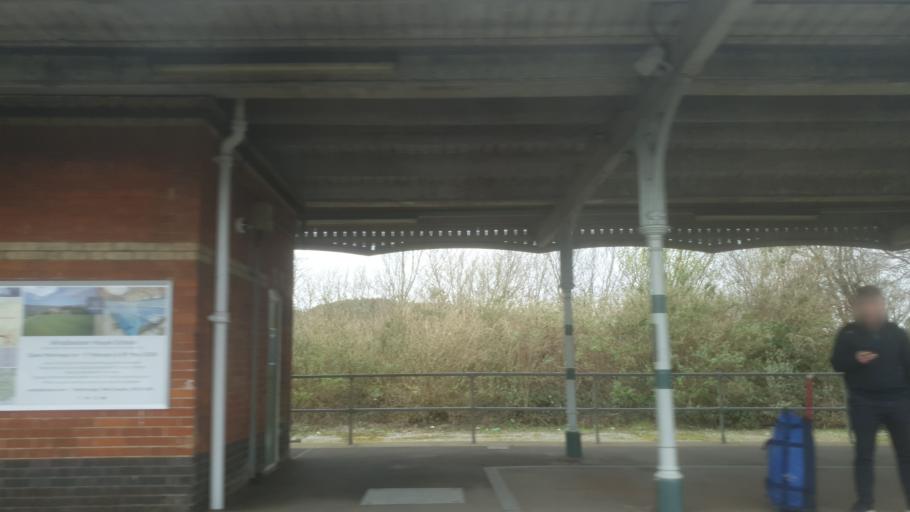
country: GB
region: England
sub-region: West Sussex
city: Pulborough
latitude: 50.9579
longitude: -0.5162
